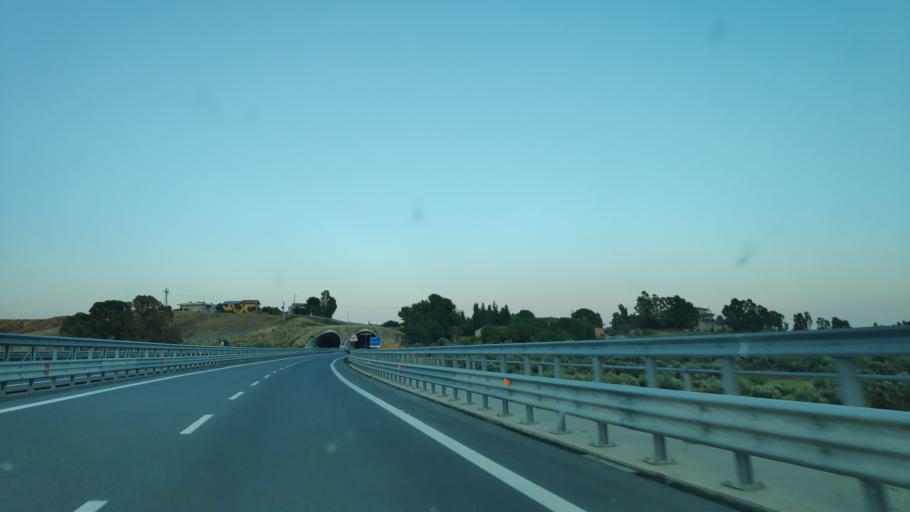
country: IT
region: Calabria
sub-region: Provincia di Reggio Calabria
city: Marina di Gioiosa Ionica
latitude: 38.3122
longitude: 16.3405
